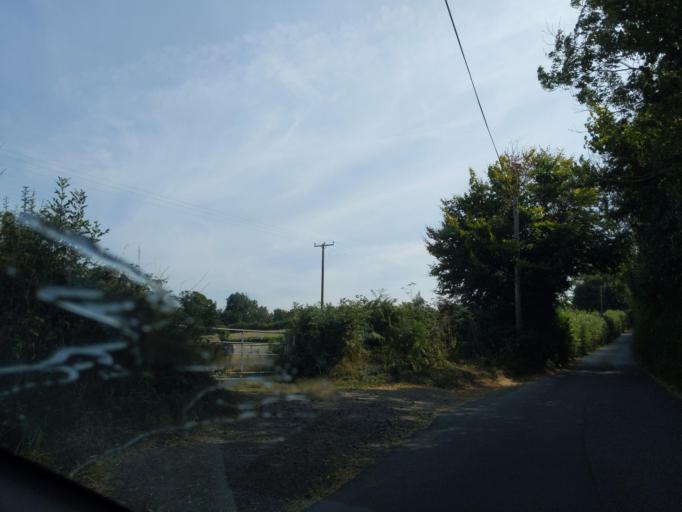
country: GB
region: England
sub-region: Devon
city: Winkleigh
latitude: 50.8806
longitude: -3.8728
